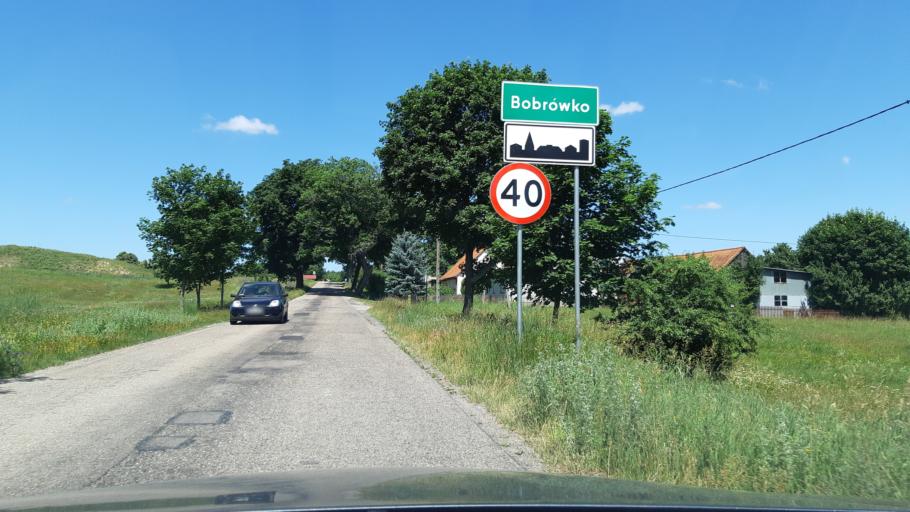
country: PL
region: Warmian-Masurian Voivodeship
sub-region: Powiat mragowski
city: Mikolajki
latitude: 53.7344
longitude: 21.5056
